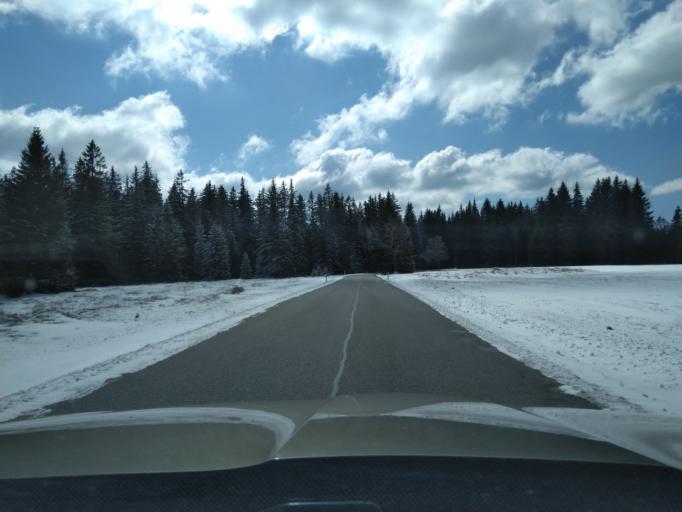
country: CZ
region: Jihocesky
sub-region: Okres Prachatice
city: Borova Lada
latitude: 49.0434
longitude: 13.5786
